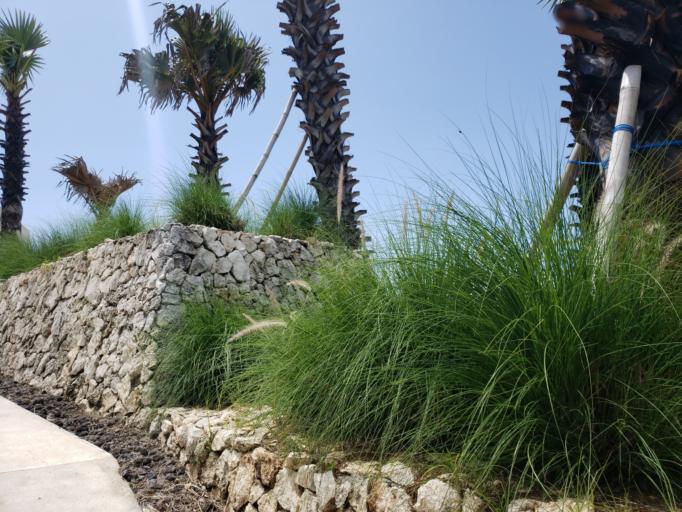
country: ID
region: Bali
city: Kangin
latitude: -8.8443
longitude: 115.1296
